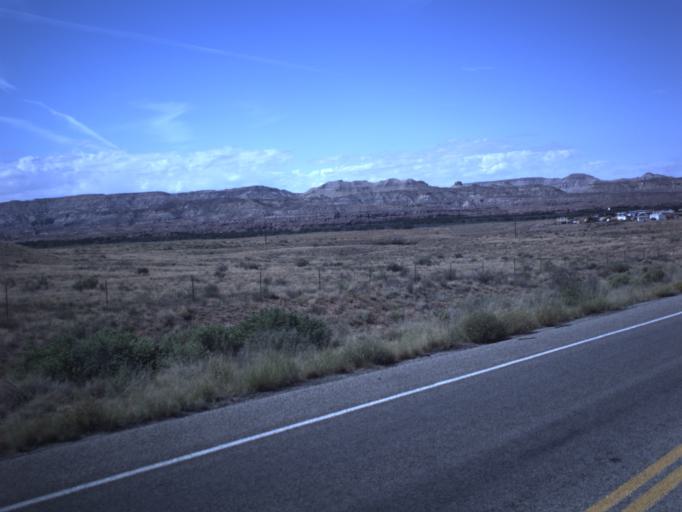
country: US
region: Colorado
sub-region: Montezuma County
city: Towaoc
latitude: 37.1947
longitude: -109.1445
